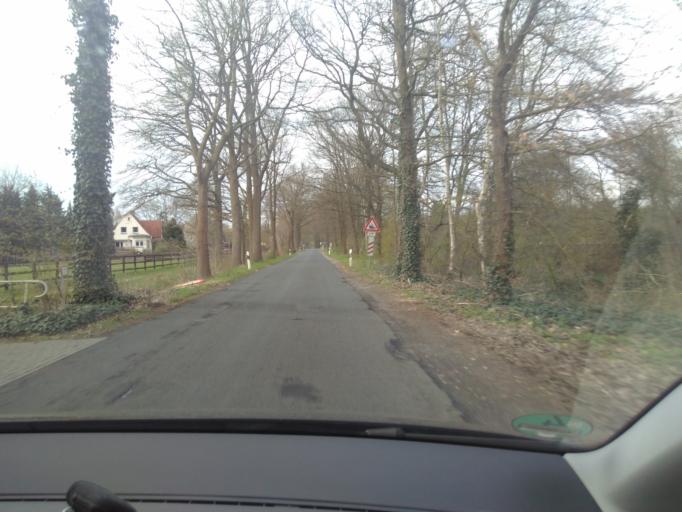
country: DE
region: Lower Saxony
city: Adelheidsdorf
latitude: 52.5417
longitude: 10.0355
